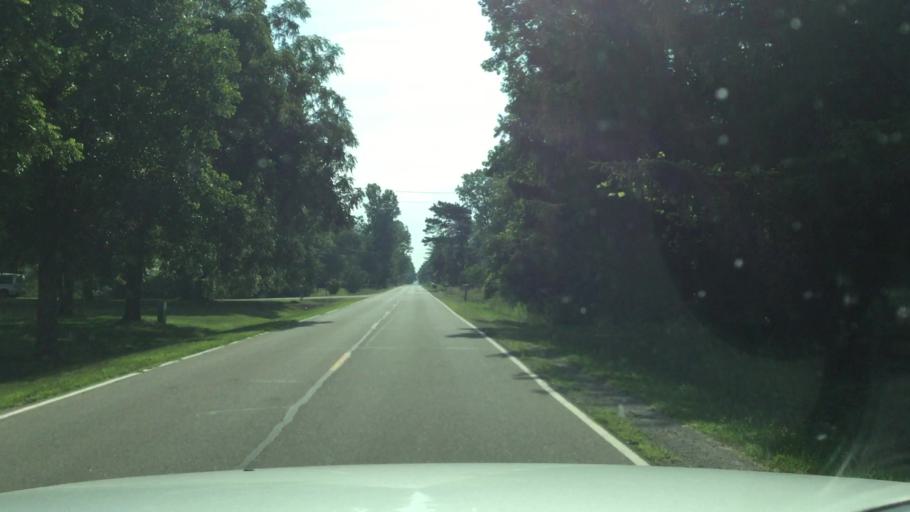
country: US
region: Michigan
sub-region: Genesee County
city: Montrose
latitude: 43.1333
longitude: -83.8440
